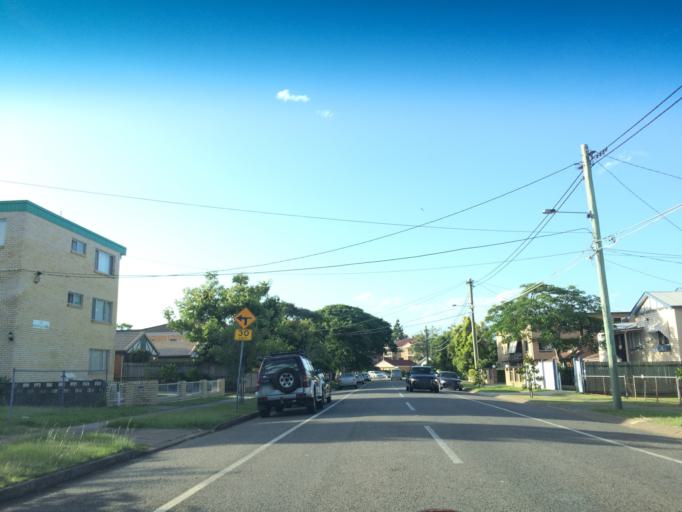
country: AU
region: Queensland
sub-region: Brisbane
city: Seven Hills
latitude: -27.4908
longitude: 153.0591
